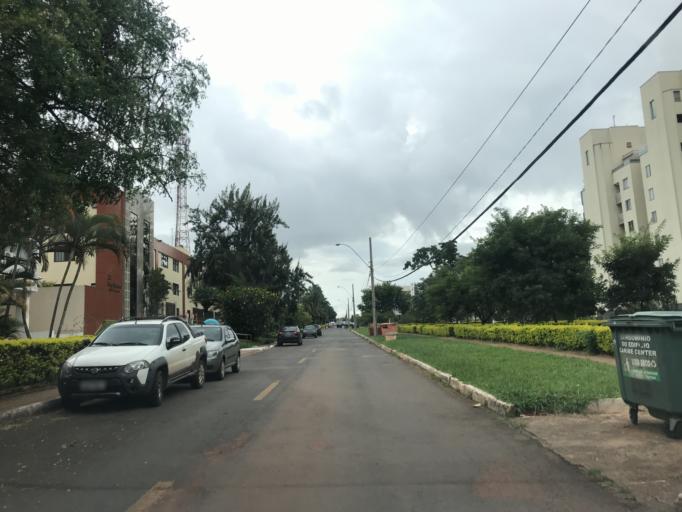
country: BR
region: Federal District
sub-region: Brasilia
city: Brasilia
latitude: -15.7923
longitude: -47.9195
